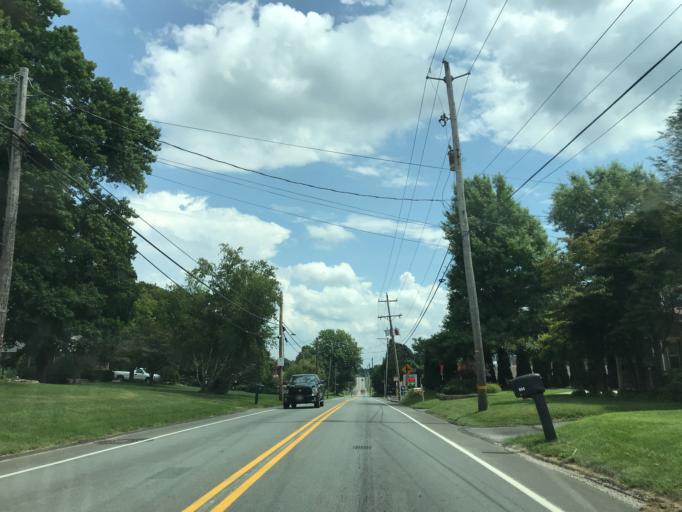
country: US
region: Pennsylvania
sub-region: York County
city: Windsor
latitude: 39.8980
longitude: -76.5699
